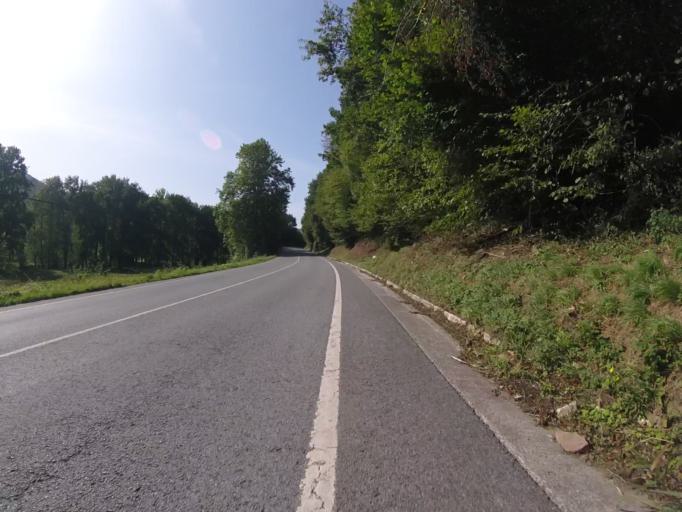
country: ES
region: Navarre
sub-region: Provincia de Navarra
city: Zugarramurdi
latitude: 43.1574
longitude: -1.5012
